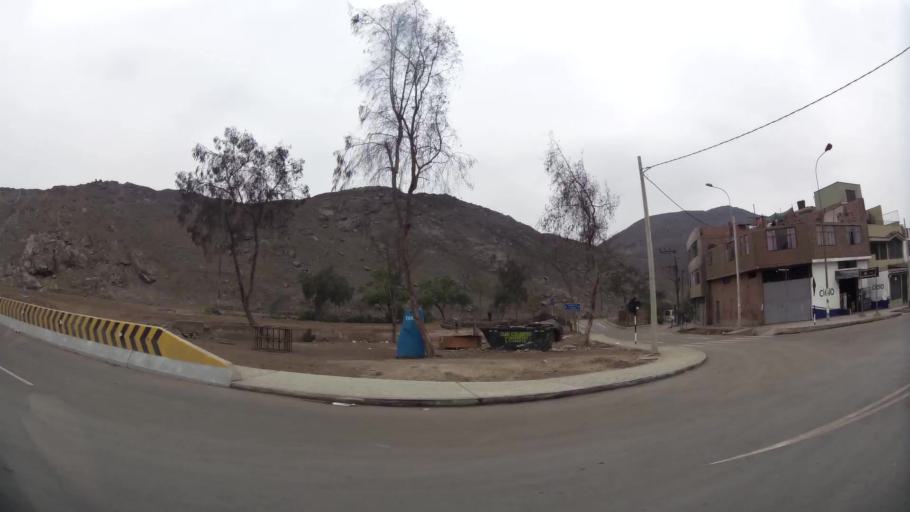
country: PE
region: Lima
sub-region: Lima
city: Vitarte
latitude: -12.0444
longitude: -76.9338
